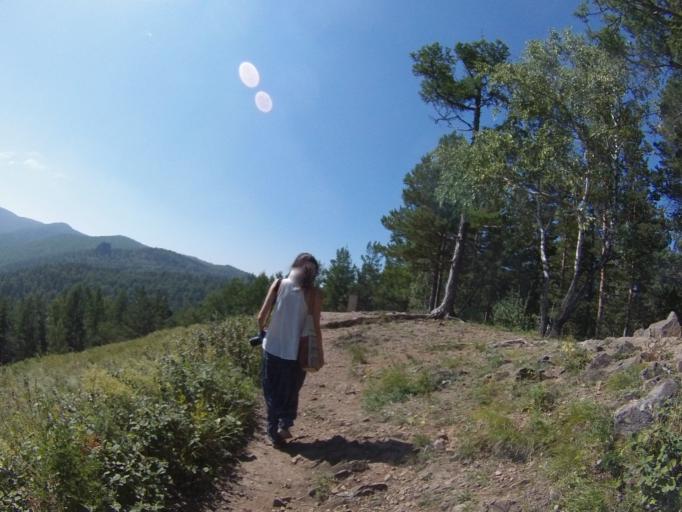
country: RU
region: Krasnoyarskiy
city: Krasnoyarsk
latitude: 55.9464
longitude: 92.7780
